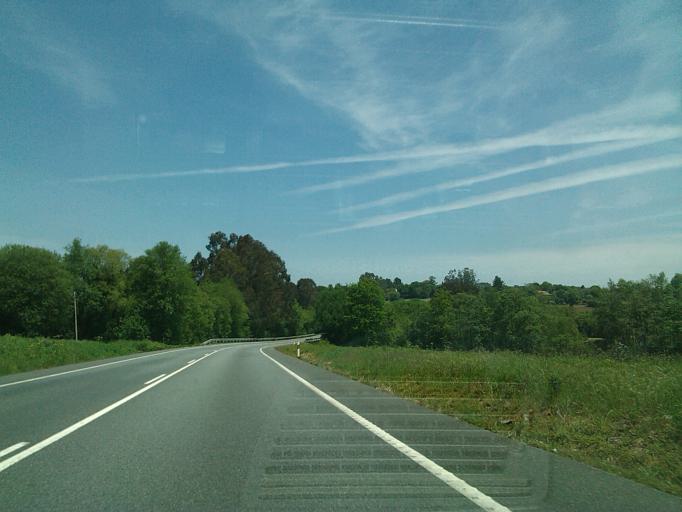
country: ES
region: Galicia
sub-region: Provincia da Coruna
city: Mesia
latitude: 43.0825
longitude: -8.1920
